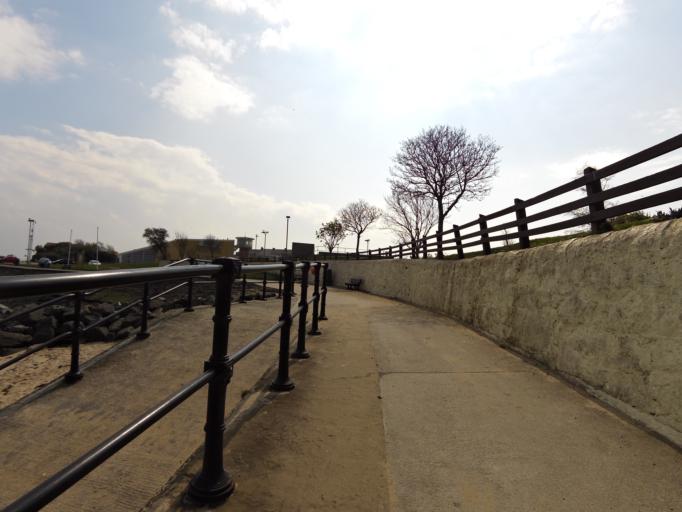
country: GB
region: Scotland
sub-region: Fife
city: Burntisland
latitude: 56.0605
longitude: -3.2257
